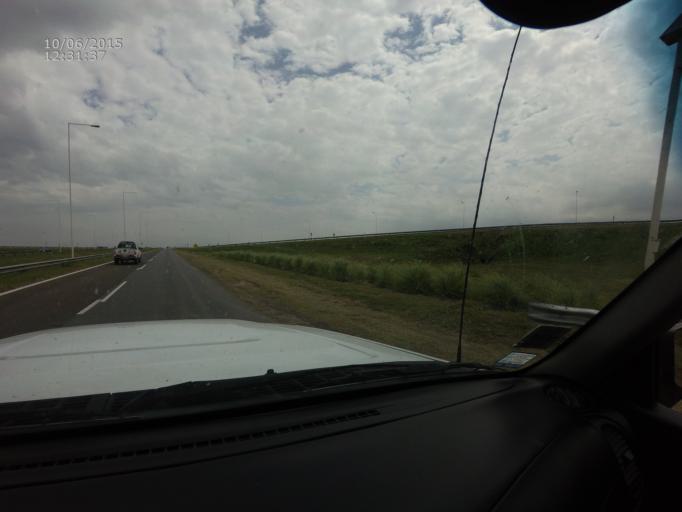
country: AR
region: Santa Fe
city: Carcarana
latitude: -32.8837
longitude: -61.1282
